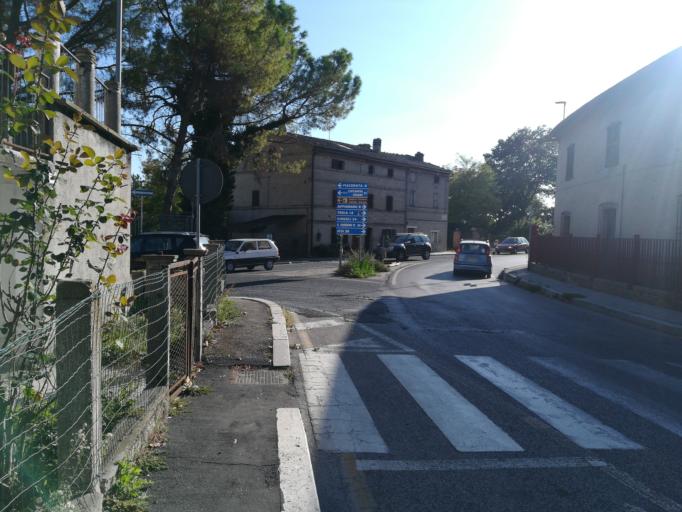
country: IT
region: The Marches
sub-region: Provincia di Macerata
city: Villa Potenza
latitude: 43.3285
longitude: 13.4237
